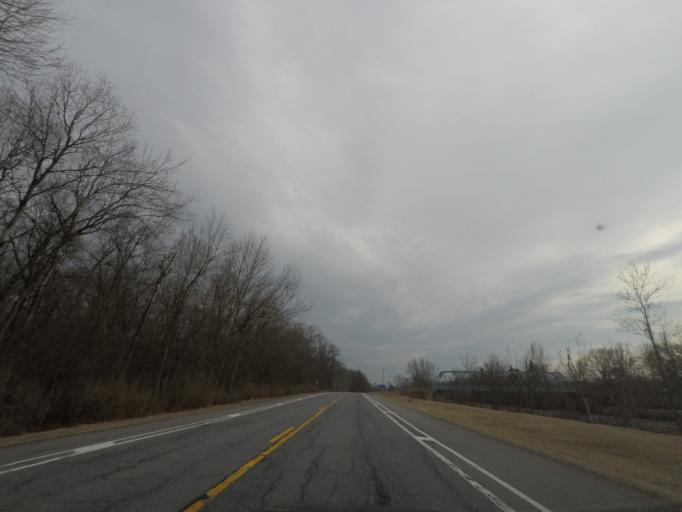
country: US
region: New York
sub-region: Saratoga County
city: Schuylerville
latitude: 43.1788
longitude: -73.5787
